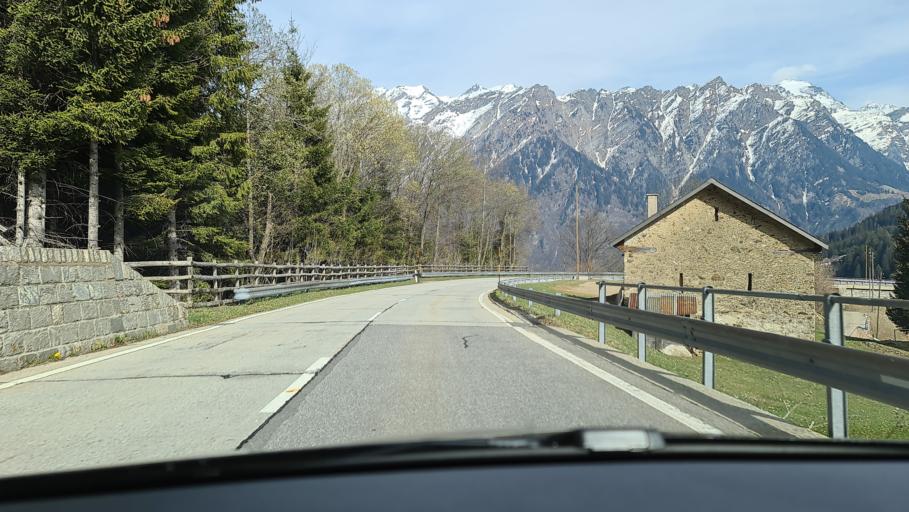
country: CH
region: Ticino
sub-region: Blenio District
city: Cancori
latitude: 46.5263
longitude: 8.9018
